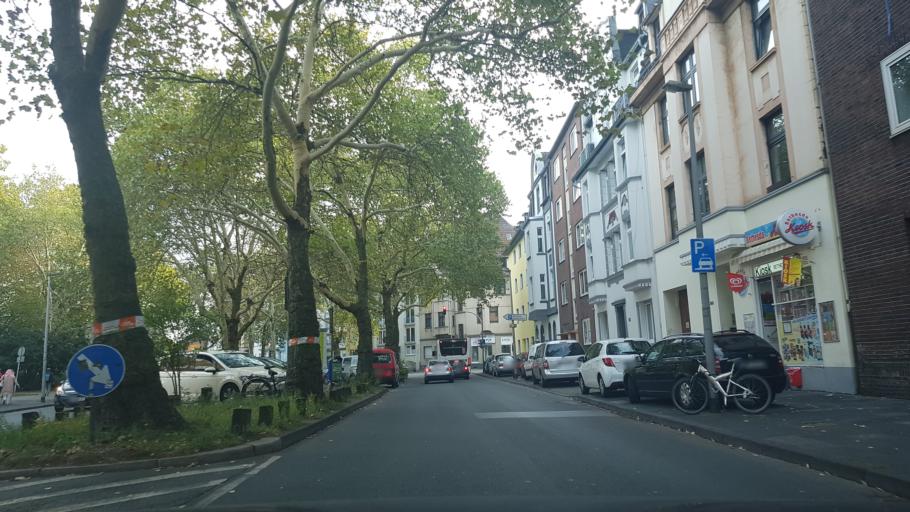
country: DE
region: North Rhine-Westphalia
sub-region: Regierungsbezirk Dusseldorf
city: Hochfeld
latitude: 51.4167
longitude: 6.7601
